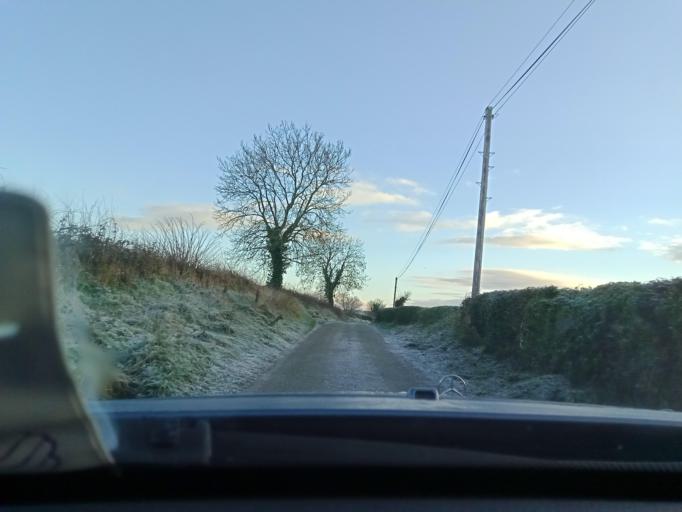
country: IE
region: Leinster
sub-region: County Carlow
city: Bagenalstown
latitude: 52.6393
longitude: -7.0120
